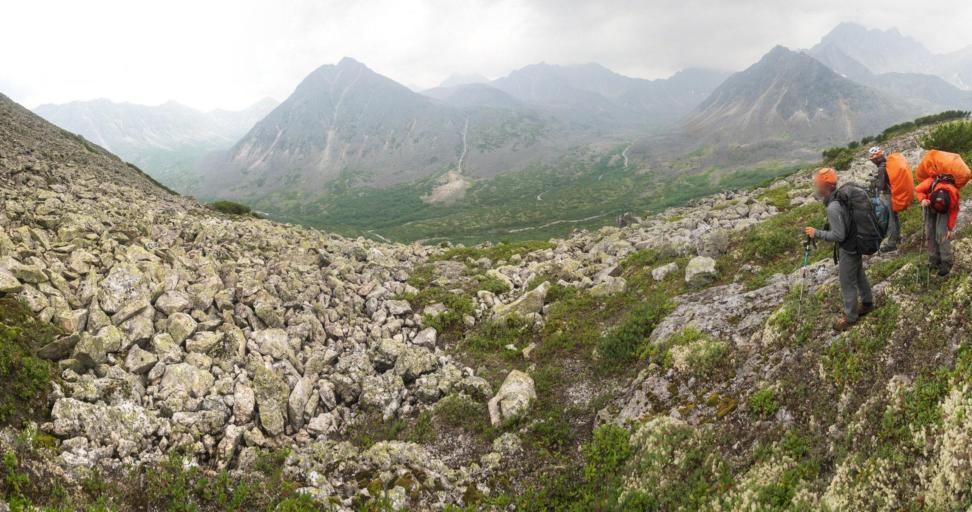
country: RU
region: Transbaikal Territory
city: Kuanda
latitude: 56.7784
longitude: 116.7415
